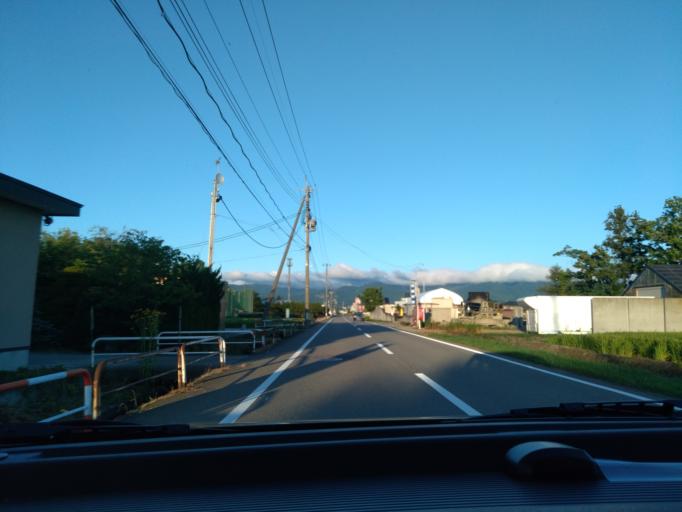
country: JP
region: Akita
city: Omagari
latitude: 39.4863
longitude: 140.5368
